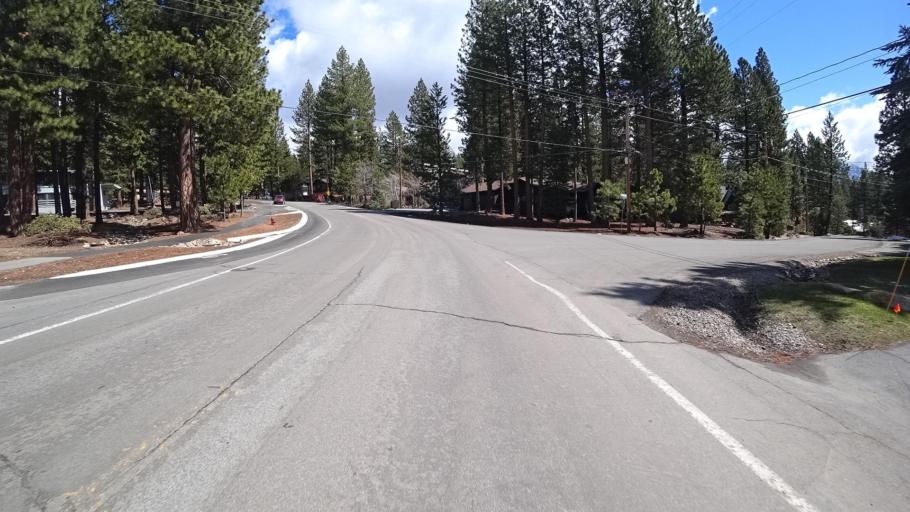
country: US
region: Nevada
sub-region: Washoe County
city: Incline Village
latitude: 39.2468
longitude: -119.9623
